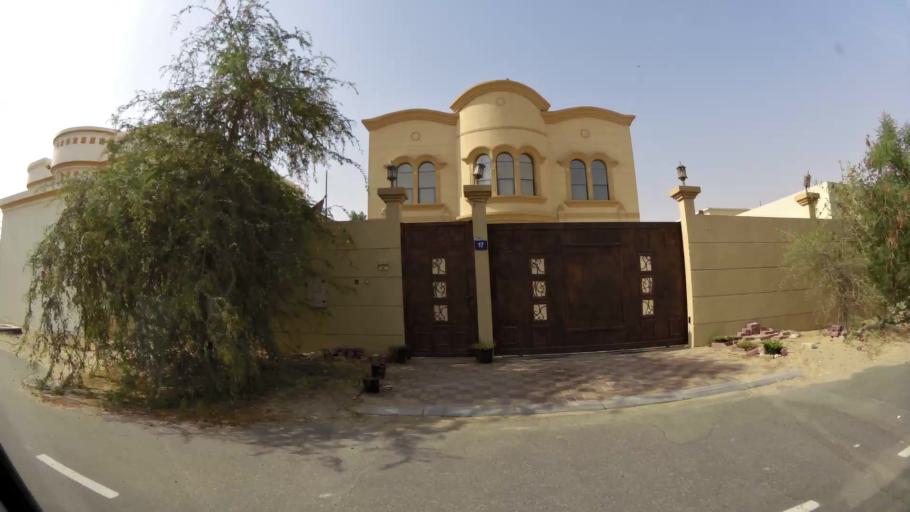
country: AE
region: Ash Shariqah
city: Sharjah
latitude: 25.2621
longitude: 55.4622
